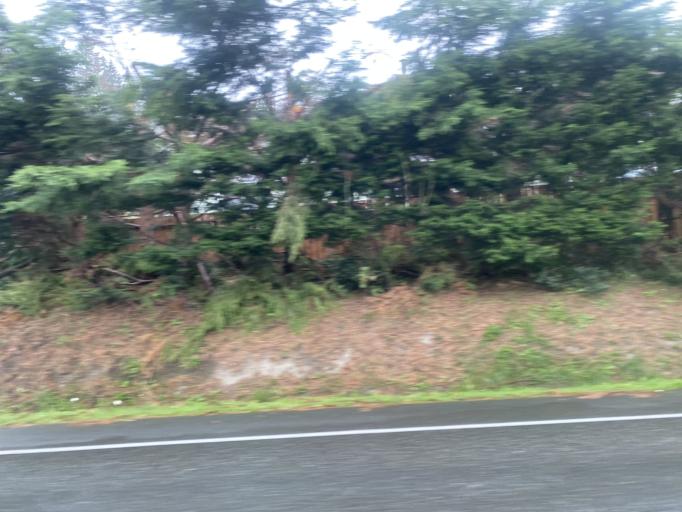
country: US
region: Washington
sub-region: Island County
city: Freeland
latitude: 48.0139
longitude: -122.5248
